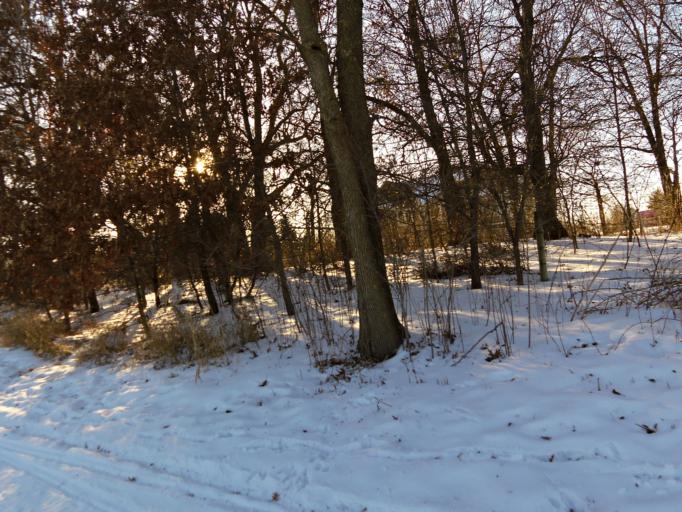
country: US
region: Minnesota
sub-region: Washington County
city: Lake Elmo
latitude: 44.9898
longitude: -92.9133
